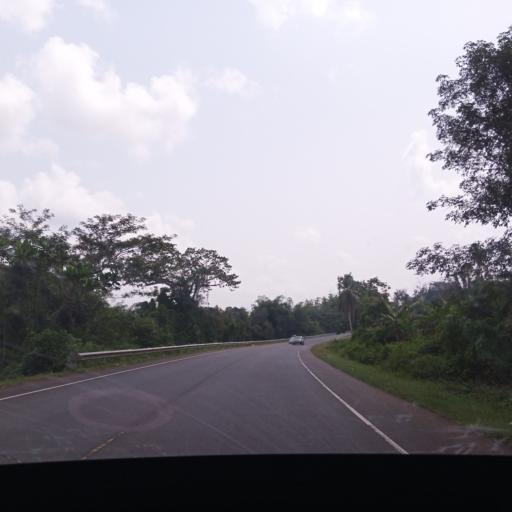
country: LR
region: Margibi
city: Kakata
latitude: 6.2422
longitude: -10.2871
